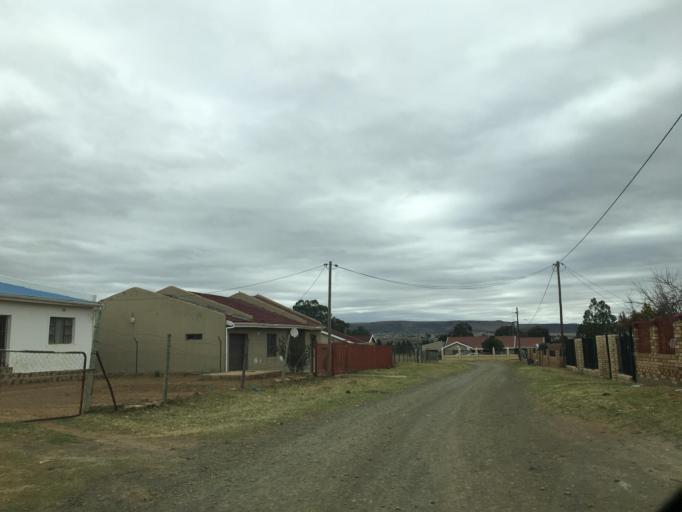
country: ZA
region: Eastern Cape
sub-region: Chris Hani District Municipality
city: Cala
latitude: -31.5335
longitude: 27.6923
